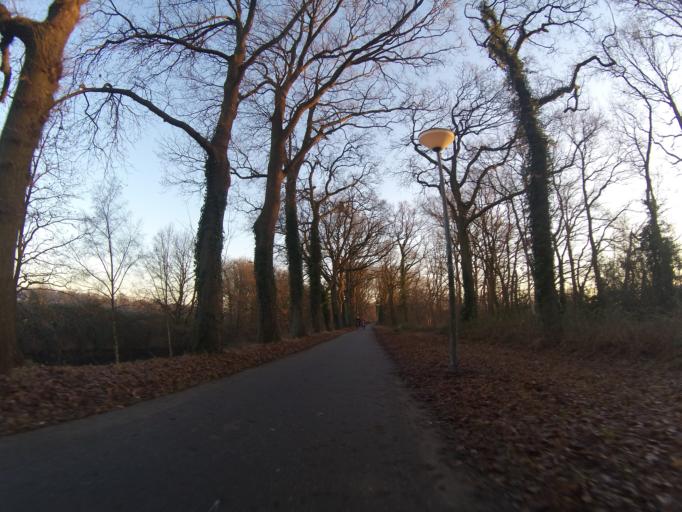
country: NL
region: Drenthe
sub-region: Gemeente Emmen
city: Emmen
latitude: 52.7570
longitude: 6.8937
